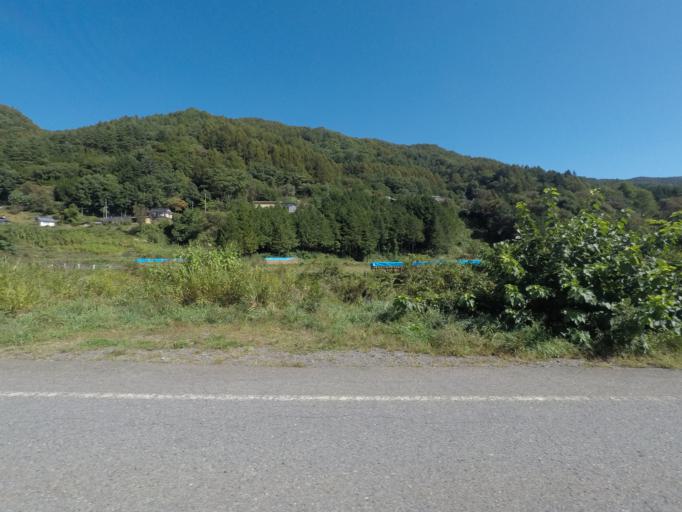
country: JP
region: Nagano
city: Tatsuno
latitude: 35.9737
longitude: 137.7526
